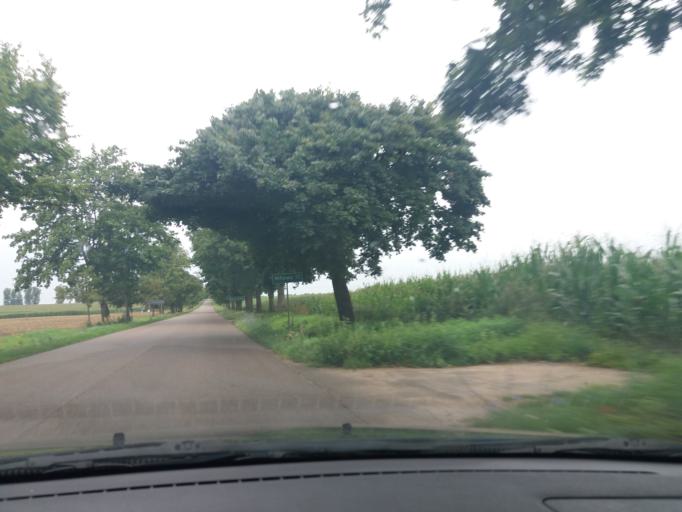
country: PL
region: Masovian Voivodeship
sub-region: Powiat mlawski
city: Wieczfnia Koscielna
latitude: 53.1913
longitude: 20.4638
